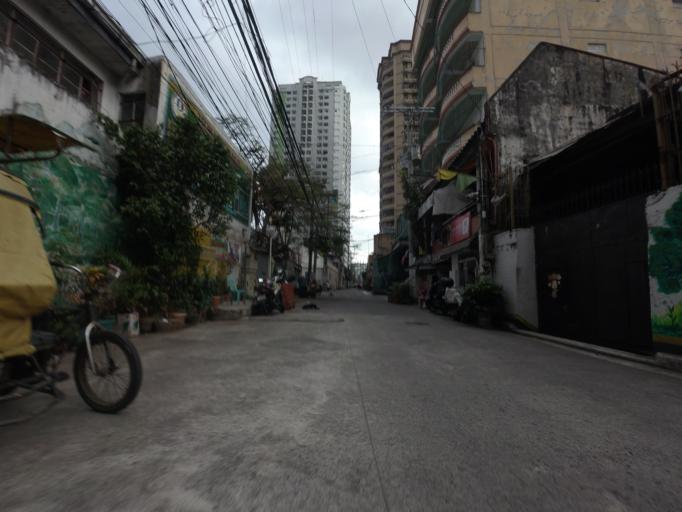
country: PH
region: Metro Manila
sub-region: City of Manila
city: Port Area
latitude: 14.5591
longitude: 120.9931
